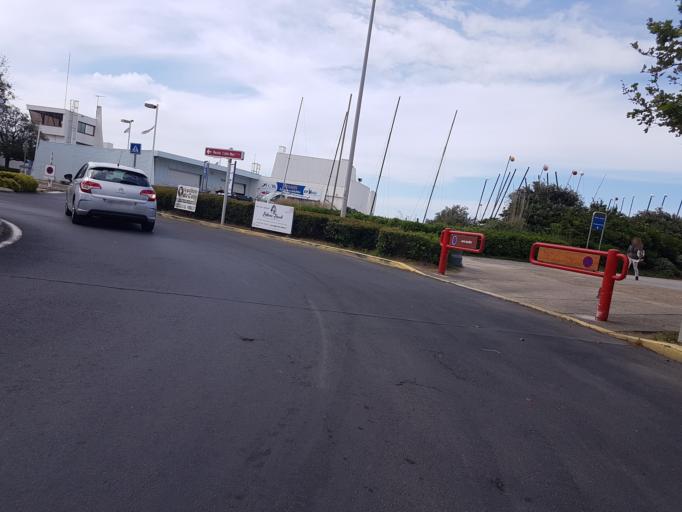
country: FR
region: Languedoc-Roussillon
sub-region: Departement de l'Herault
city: La Grande-Motte
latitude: 43.5582
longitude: 4.0753
